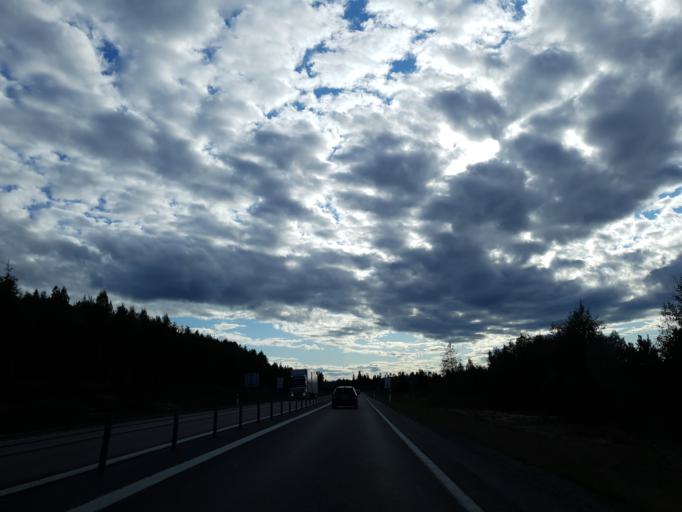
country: SE
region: Vaesternorrland
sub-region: Haernoesands Kommun
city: Haernoesand
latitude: 62.6091
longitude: 17.8316
